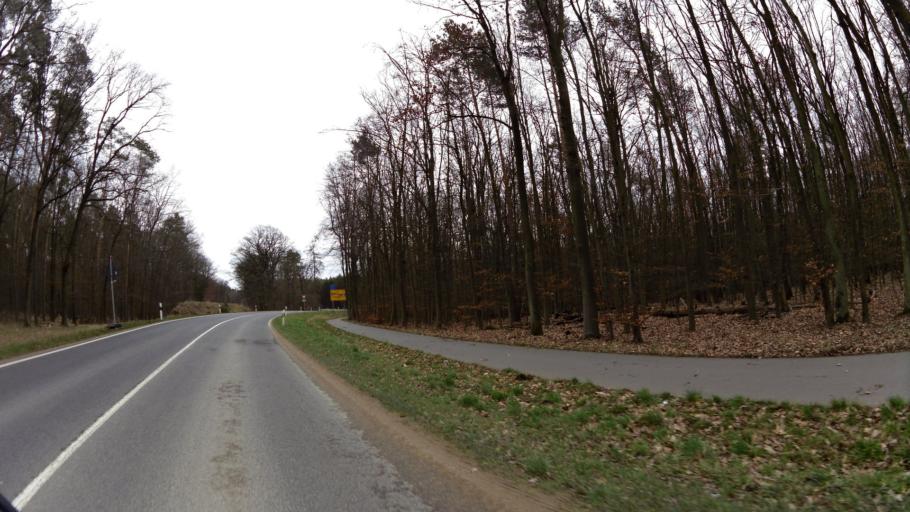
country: DE
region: Brandenburg
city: Schulzendorf
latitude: 52.3425
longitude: 13.5618
